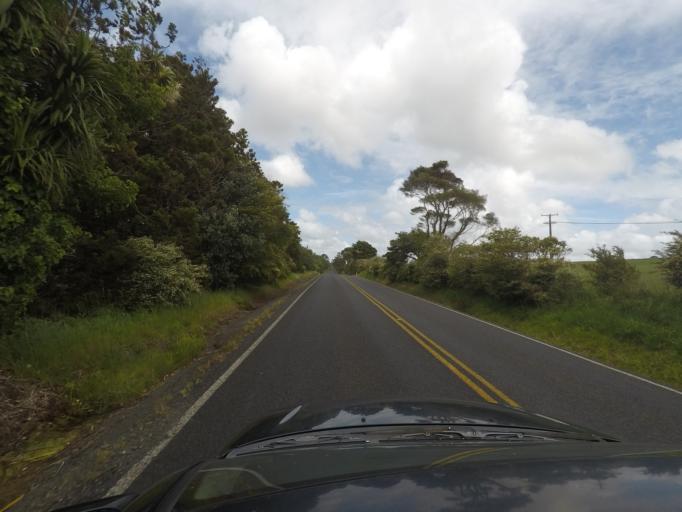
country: NZ
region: Auckland
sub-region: Auckland
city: Parakai
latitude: -36.6450
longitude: 174.5151
